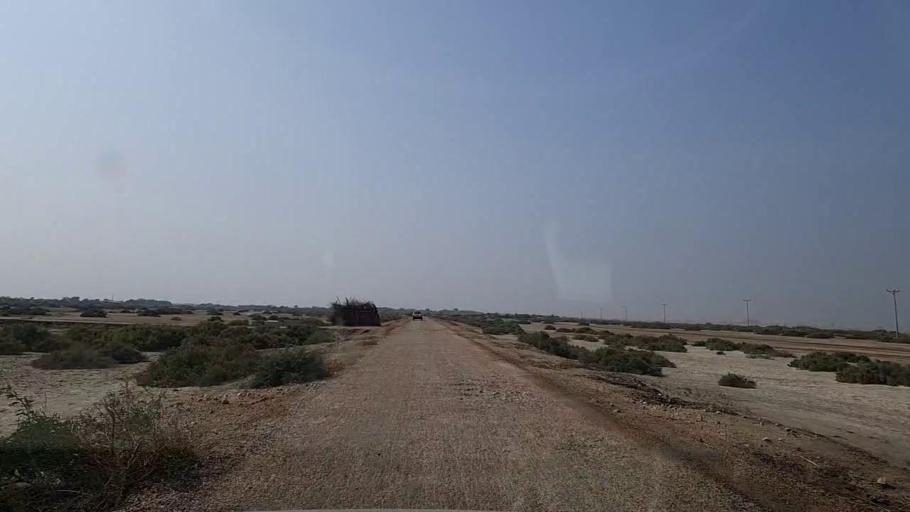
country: PK
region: Sindh
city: Mirpur Sakro
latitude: 24.5288
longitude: 67.5701
